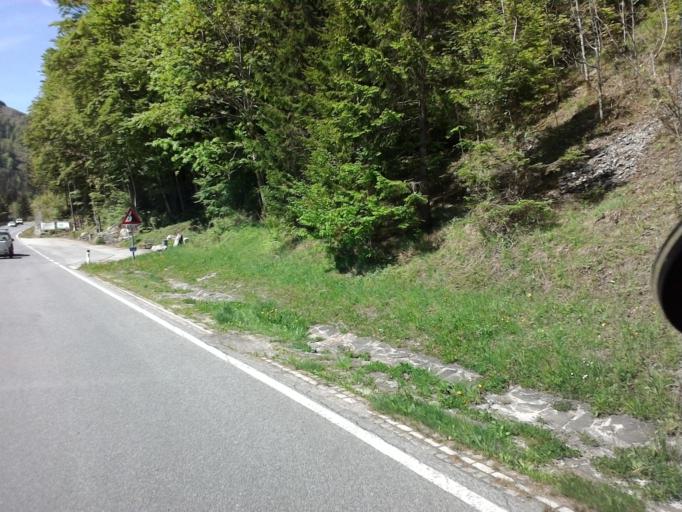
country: AT
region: Styria
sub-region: Politischer Bezirk Liezen
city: Palfau
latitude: 47.7132
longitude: 14.8305
